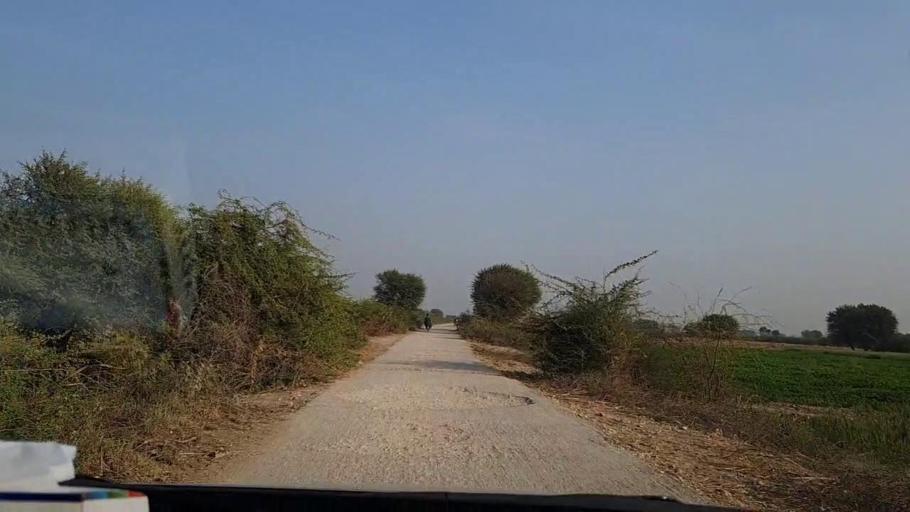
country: PK
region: Sindh
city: Tando Ghulam Ali
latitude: 25.2150
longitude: 68.8834
